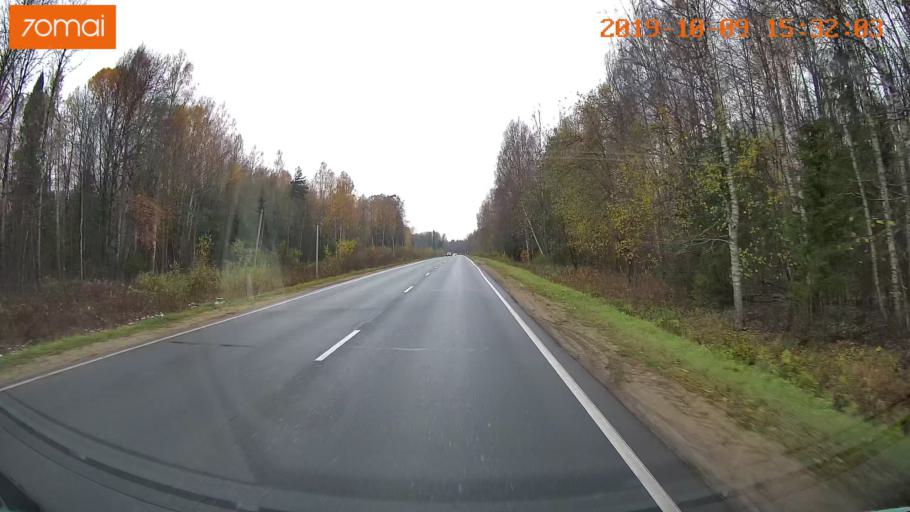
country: RU
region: Kostroma
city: Susanino
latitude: 57.9673
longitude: 41.2864
